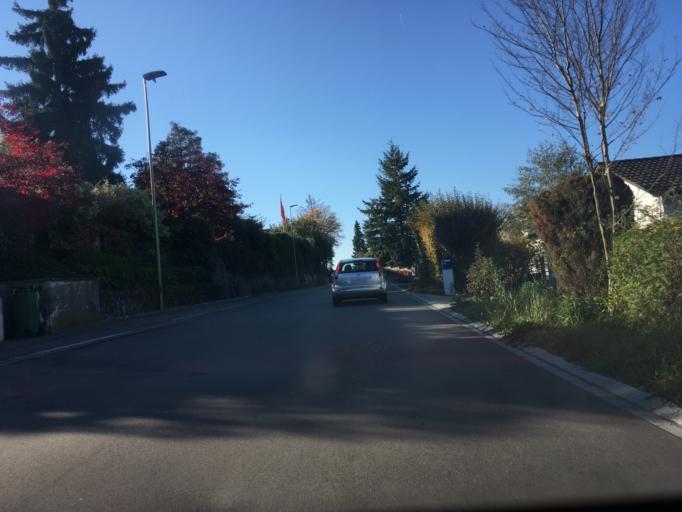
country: CH
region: Zurich
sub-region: Bezirk Dietikon
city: Uitikon
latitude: 47.3629
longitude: 8.4640
